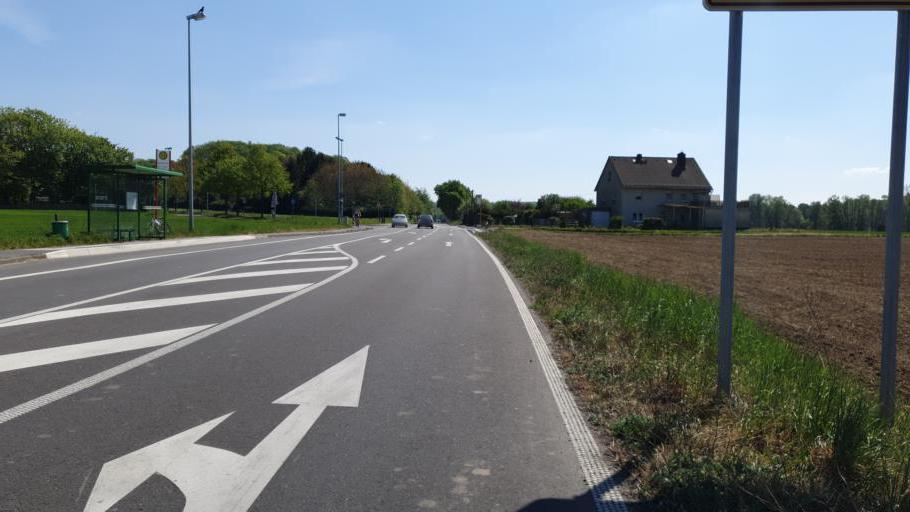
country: DE
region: North Rhine-Westphalia
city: Opladen
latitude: 51.0324
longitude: 7.0653
